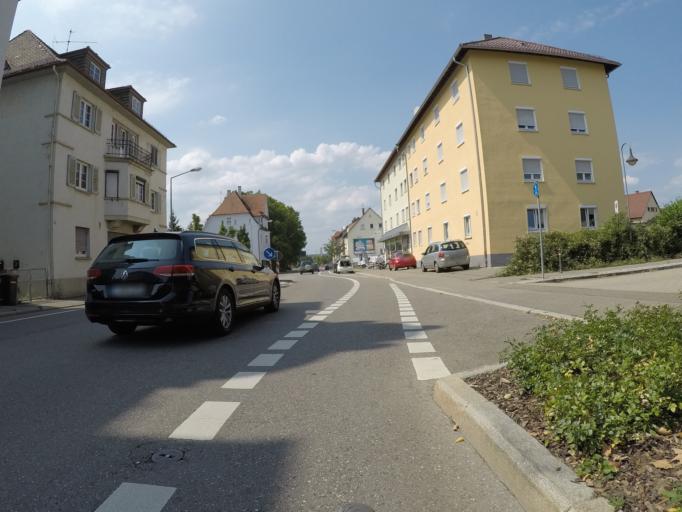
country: DE
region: Baden-Wuerttemberg
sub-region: Tuebingen Region
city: Reutlingen
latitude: 48.4940
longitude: 9.1974
